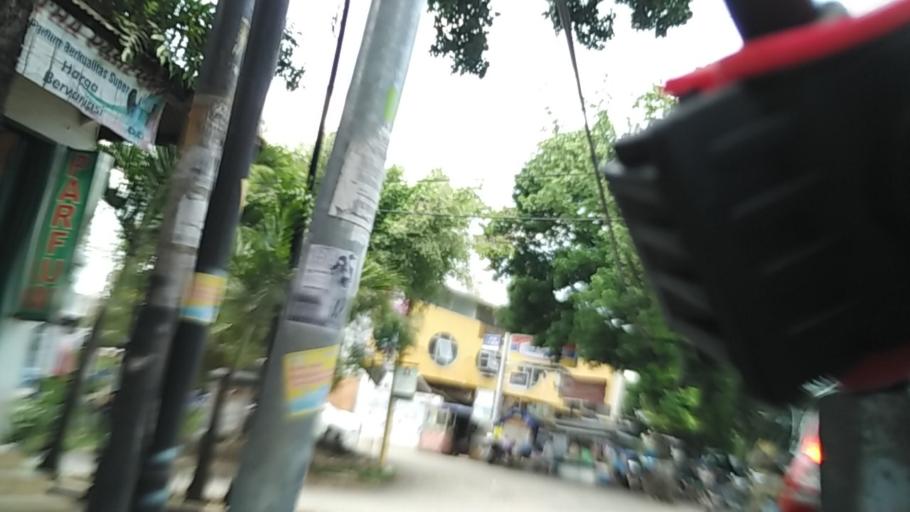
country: ID
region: Central Java
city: Semarang
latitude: -7.0110
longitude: 110.3791
